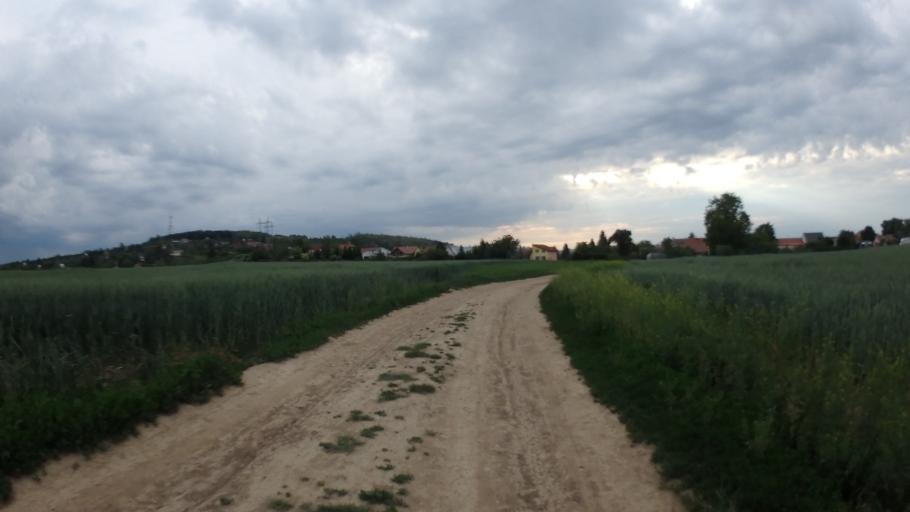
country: CZ
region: South Moravian
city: Moravany
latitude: 49.1393
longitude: 16.5576
